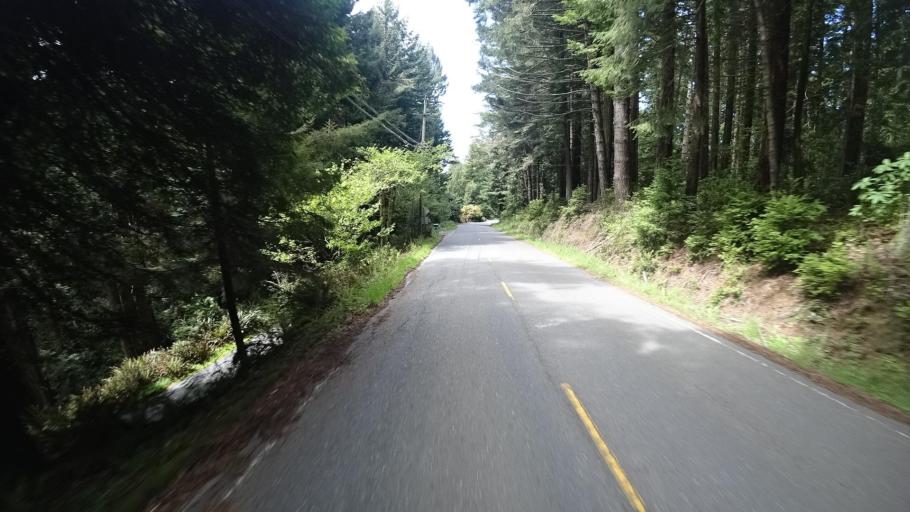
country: US
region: California
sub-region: Humboldt County
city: Arcata
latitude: 40.8699
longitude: -124.0632
